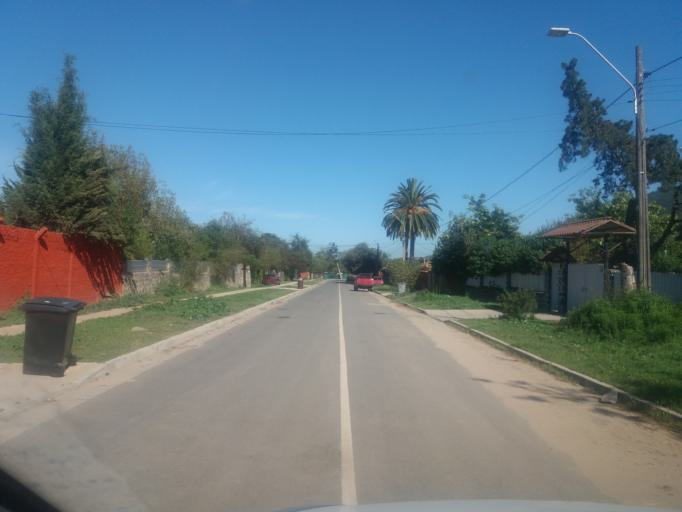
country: CL
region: Valparaiso
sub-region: Provincia de Marga Marga
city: Limache
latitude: -32.9899
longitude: -71.1618
